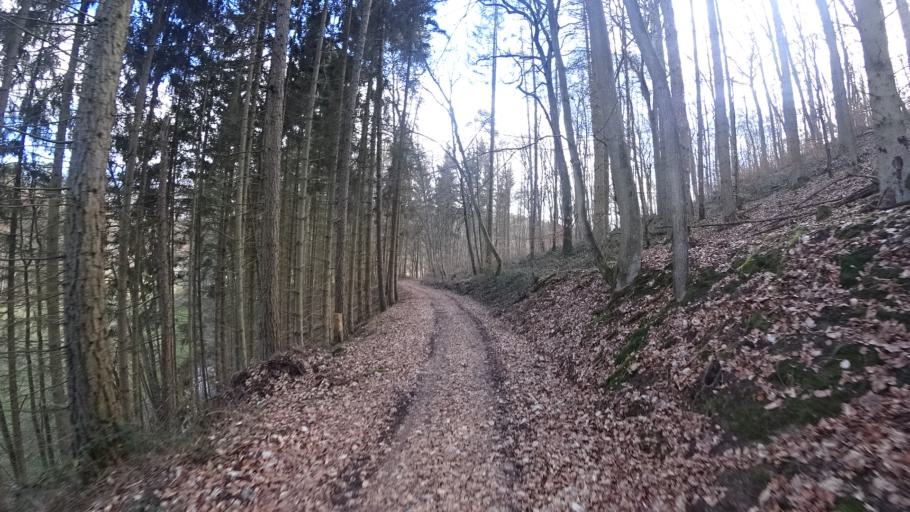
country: DE
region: Rheinland-Pfalz
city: Bornich
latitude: 50.1409
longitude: 7.7539
